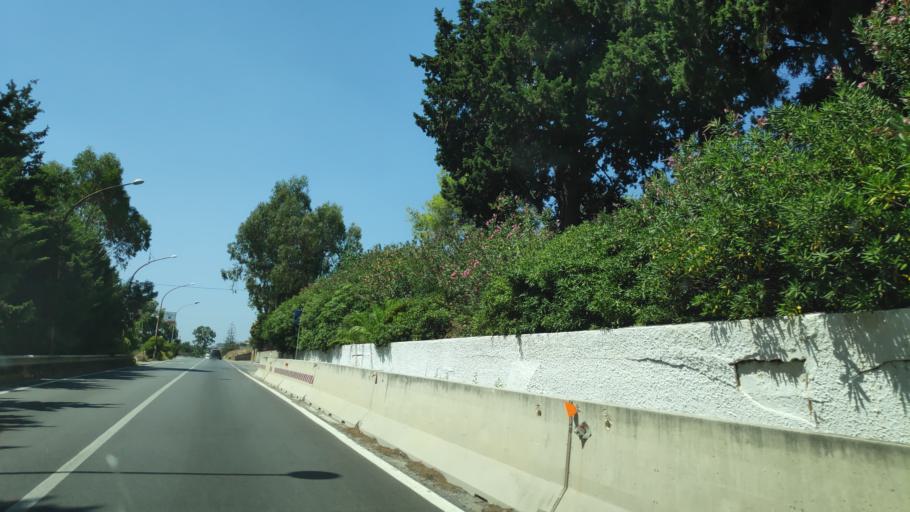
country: IT
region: Calabria
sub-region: Provincia di Reggio Calabria
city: Weather Station
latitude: 37.9576
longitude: 16.0958
